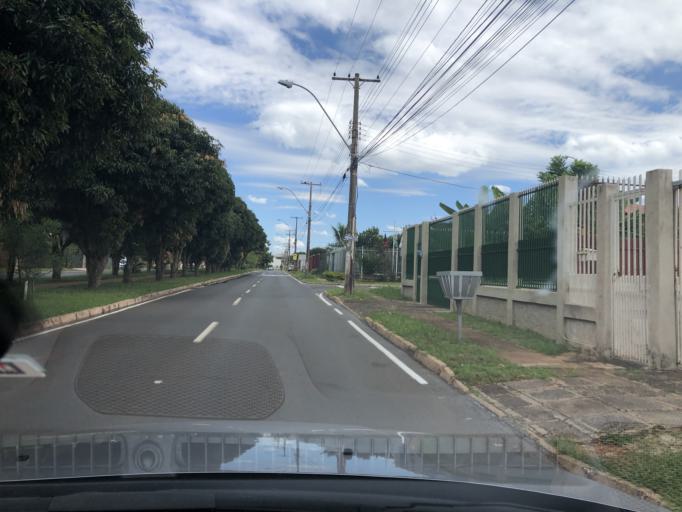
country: BR
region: Federal District
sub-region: Brasilia
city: Brasilia
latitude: -15.9926
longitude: -47.9895
